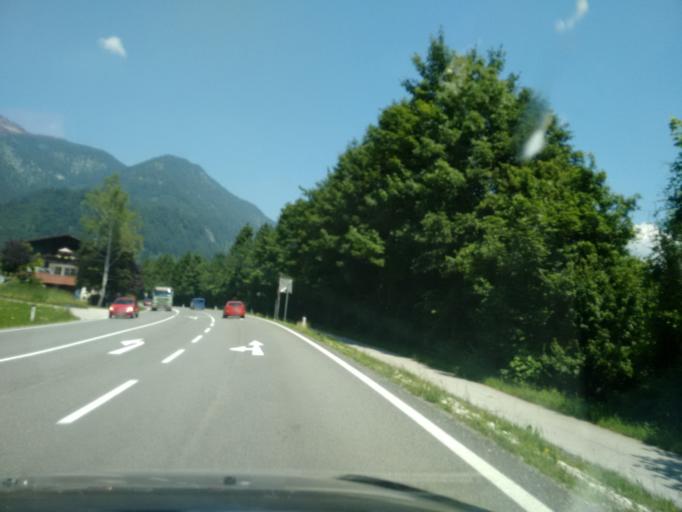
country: AT
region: Upper Austria
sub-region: Politischer Bezirk Gmunden
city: Ebensee
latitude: 47.7762
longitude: 13.7290
